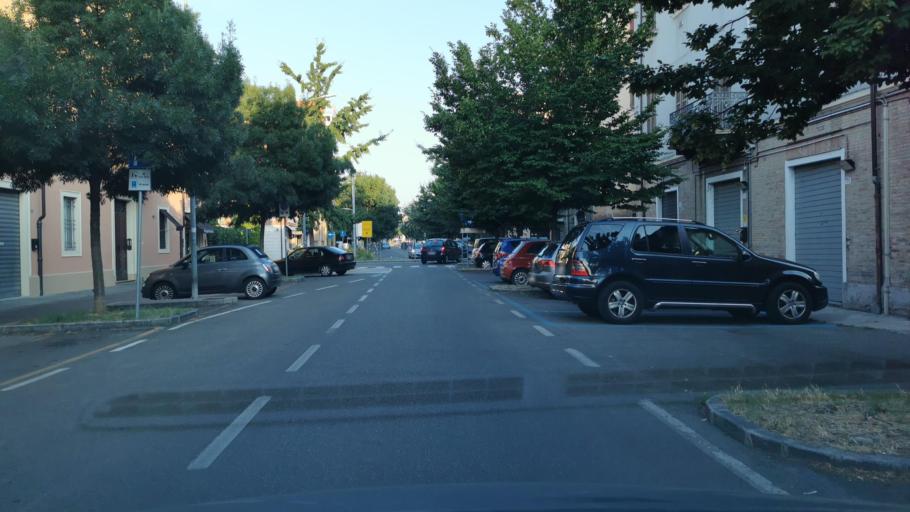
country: IT
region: Emilia-Romagna
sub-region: Provincia di Modena
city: Modena
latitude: 44.6512
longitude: 10.9358
